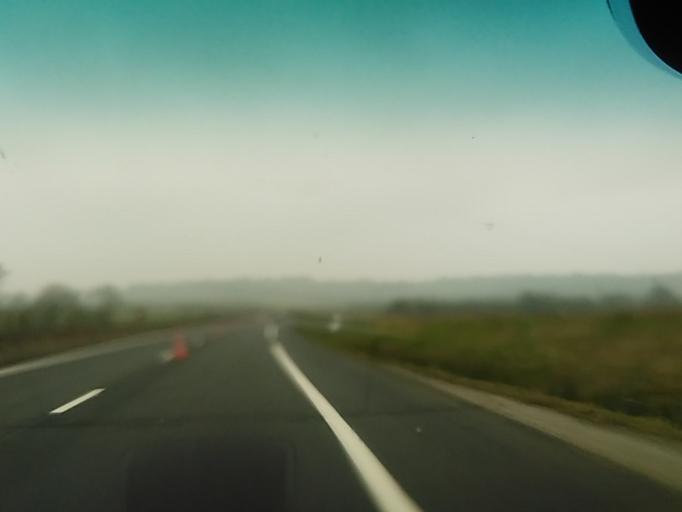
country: FR
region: Lower Normandy
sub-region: Departement de l'Orne
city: Gace
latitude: 48.7174
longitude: 0.2567
